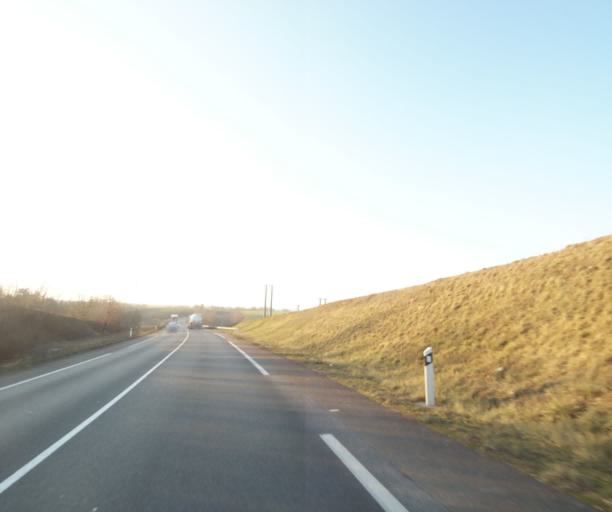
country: FR
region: Champagne-Ardenne
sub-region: Departement de la Haute-Marne
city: Bienville
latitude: 48.5457
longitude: 5.0753
